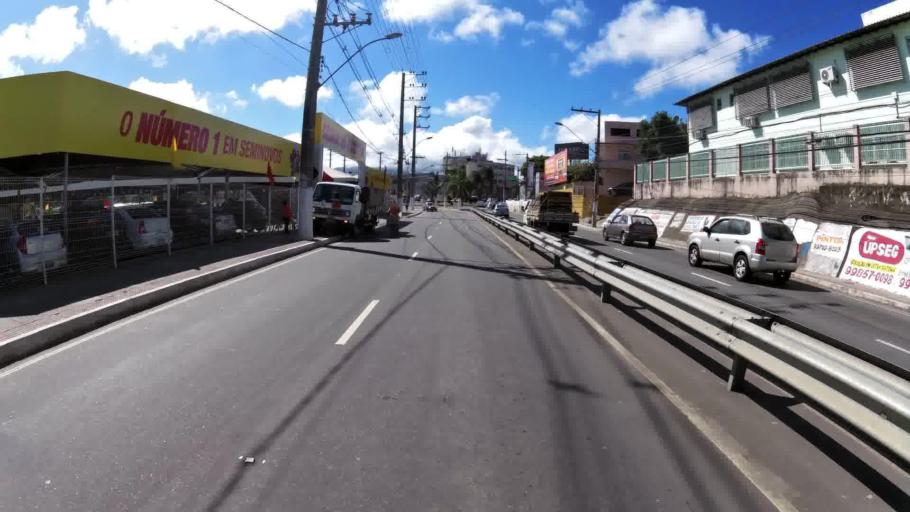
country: BR
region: Espirito Santo
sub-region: Vila Velha
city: Vila Velha
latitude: -20.2379
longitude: -40.2770
